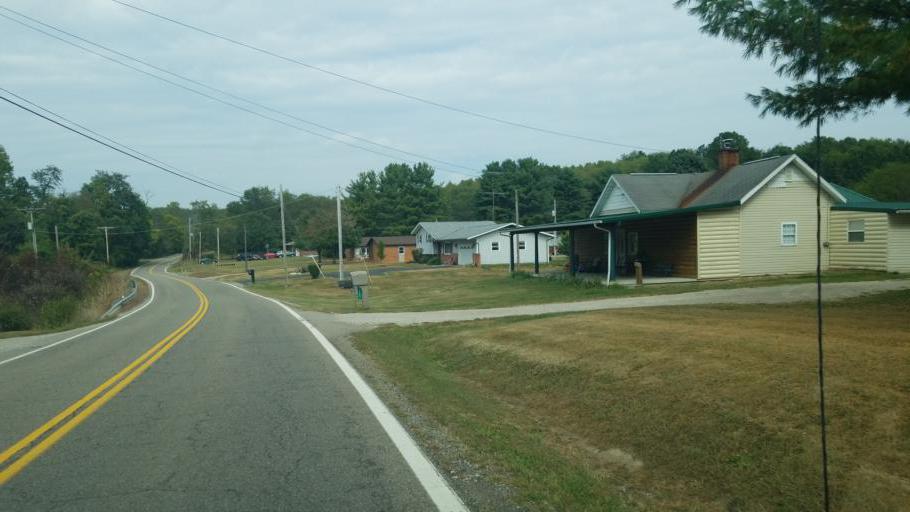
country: US
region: Ohio
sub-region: Licking County
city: Newark
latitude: 40.0507
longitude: -82.2903
